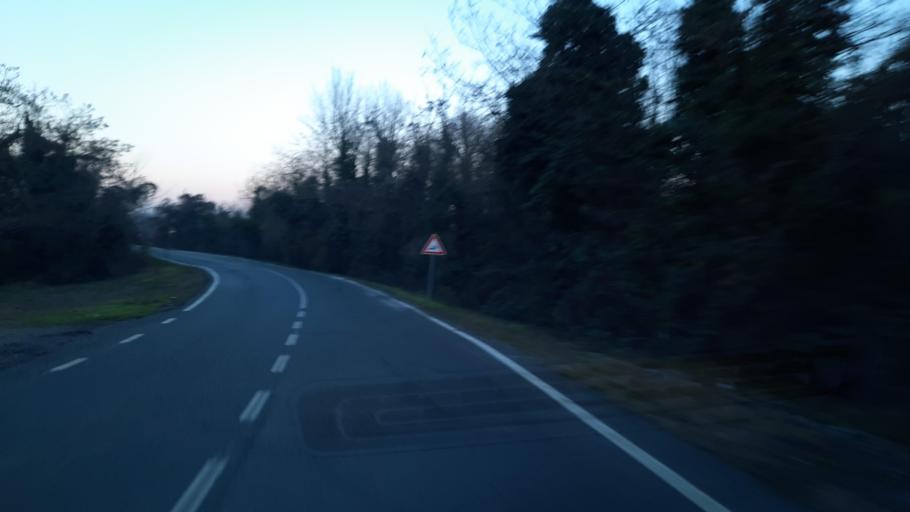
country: IT
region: Piedmont
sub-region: Provincia di Alessandria
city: Camino
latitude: 45.1717
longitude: 8.2879
